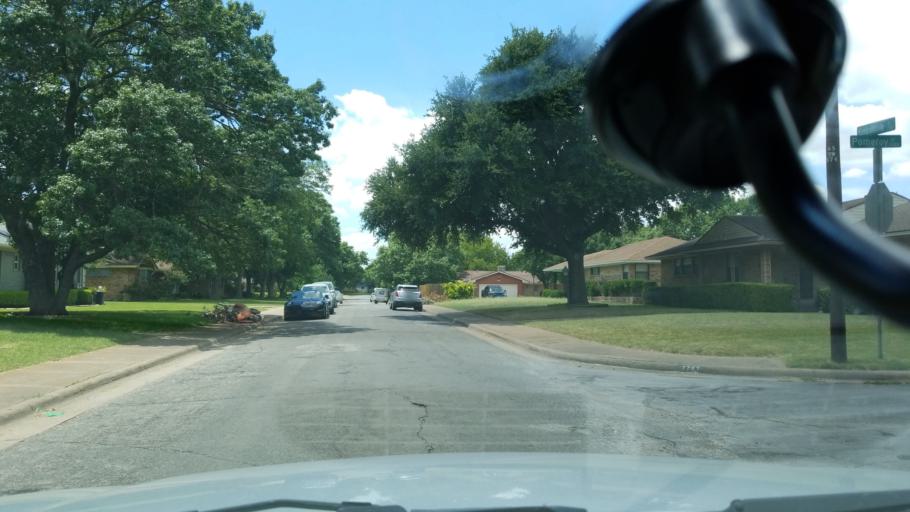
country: US
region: Texas
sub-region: Dallas County
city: Cockrell Hill
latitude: 32.6960
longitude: -96.8806
